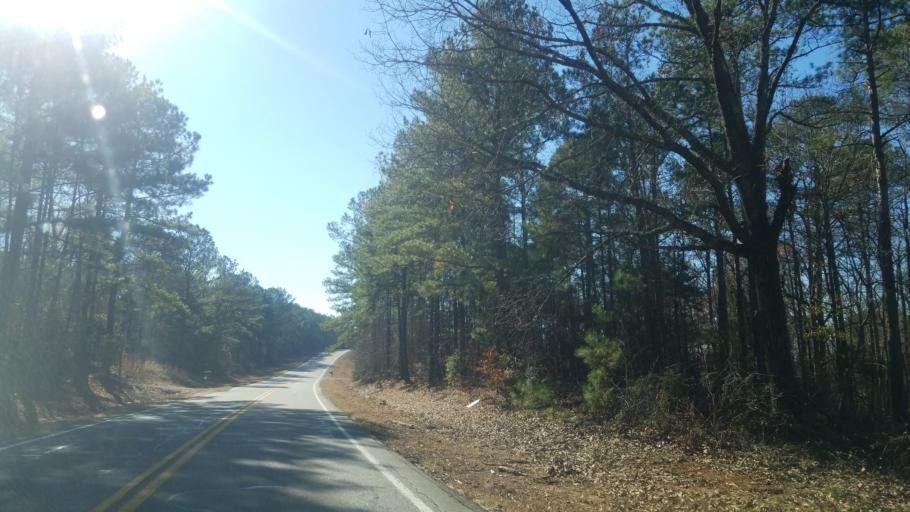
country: US
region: Georgia
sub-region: Harris County
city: Hamilton
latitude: 32.7147
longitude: -85.0225
